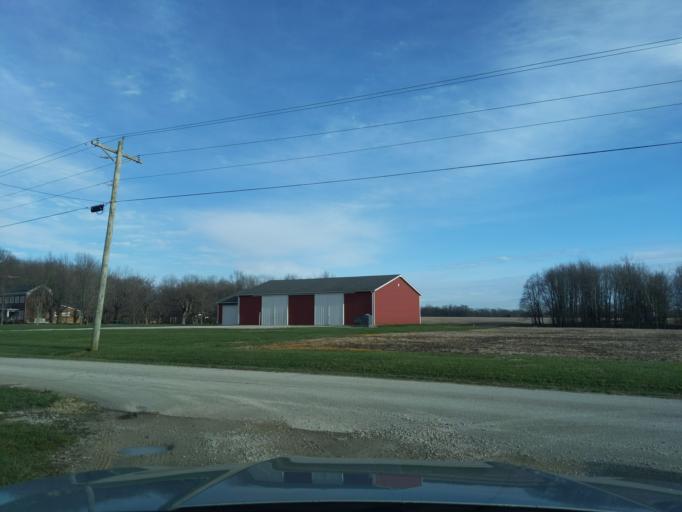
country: US
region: Indiana
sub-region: Decatur County
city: Westport
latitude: 39.2030
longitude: -85.4346
